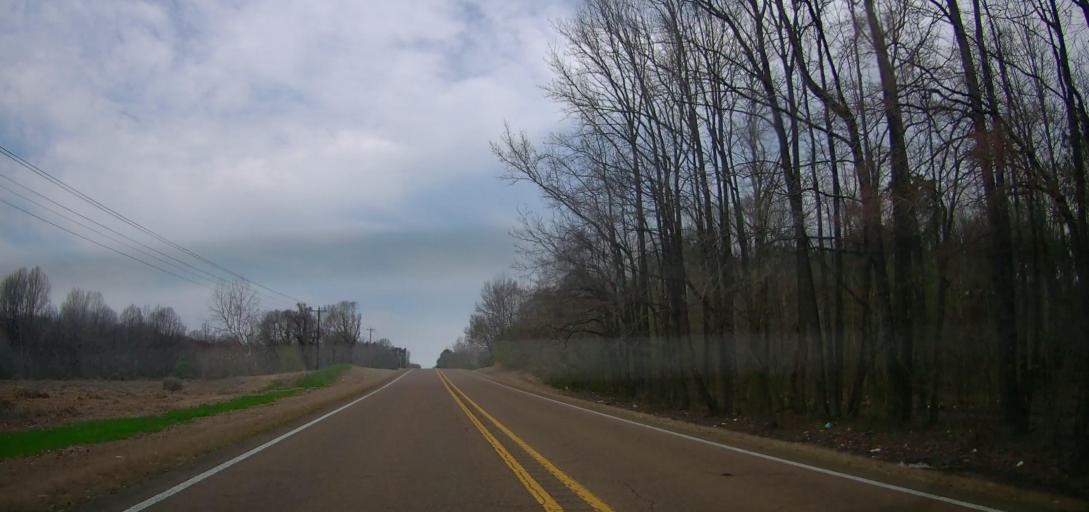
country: US
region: Mississippi
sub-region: Marshall County
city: Byhalia
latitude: 34.8518
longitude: -89.6344
